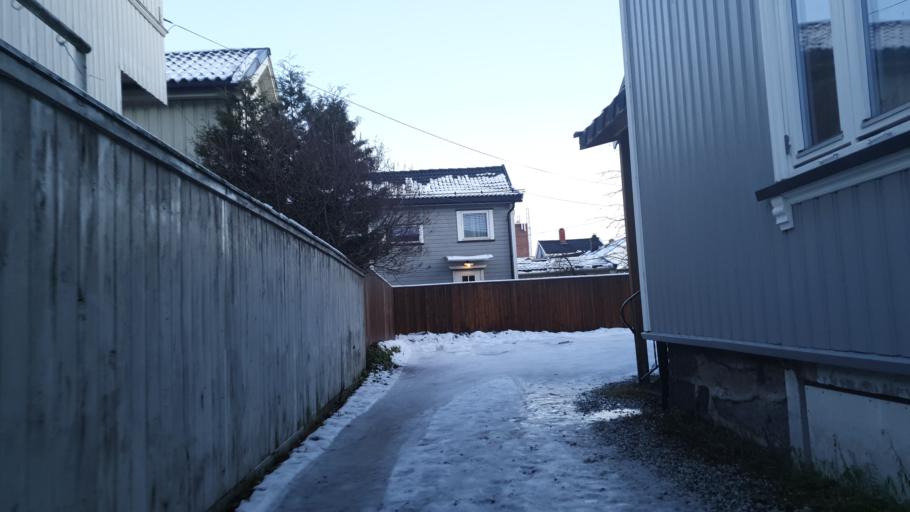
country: NO
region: Buskerud
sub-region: Drammen
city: Drammen
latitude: 59.7359
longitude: 10.2052
